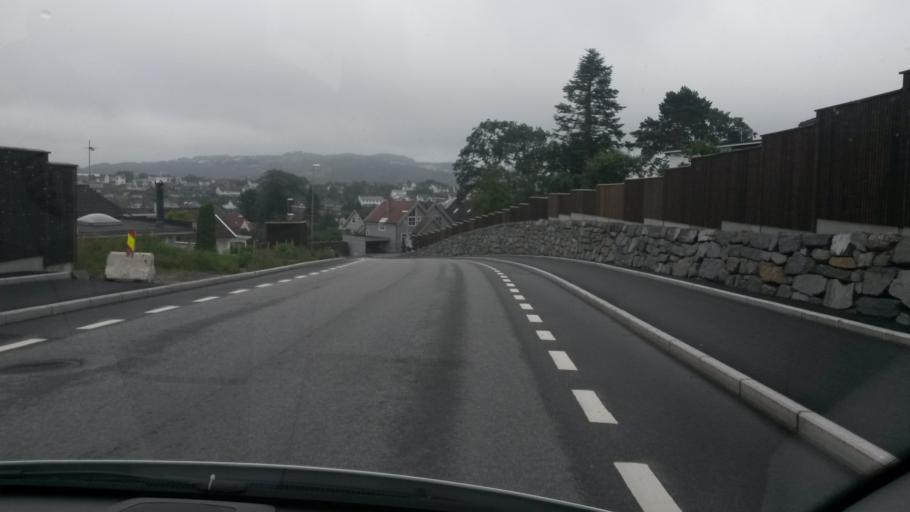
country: NO
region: Rogaland
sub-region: Sandnes
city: Sandnes
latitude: 58.8309
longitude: 5.7145
